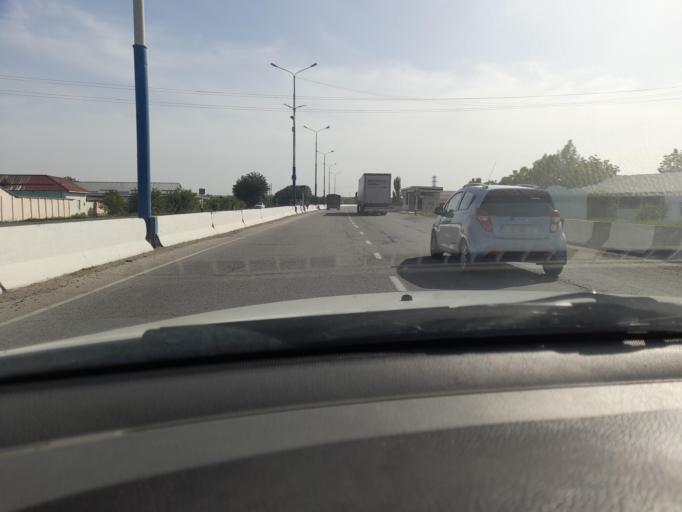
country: UZ
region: Samarqand
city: Kattaqo'rg'on
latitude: 39.9251
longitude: 66.3574
